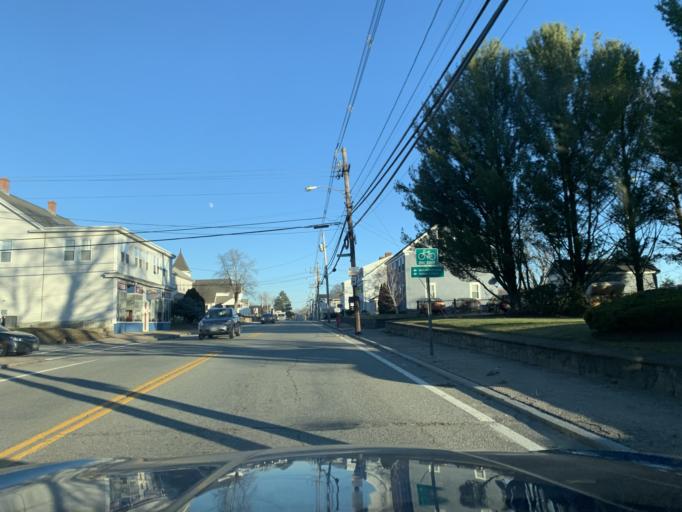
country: US
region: Rhode Island
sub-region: Kent County
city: West Warwick
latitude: 41.6954
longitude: -71.5393
